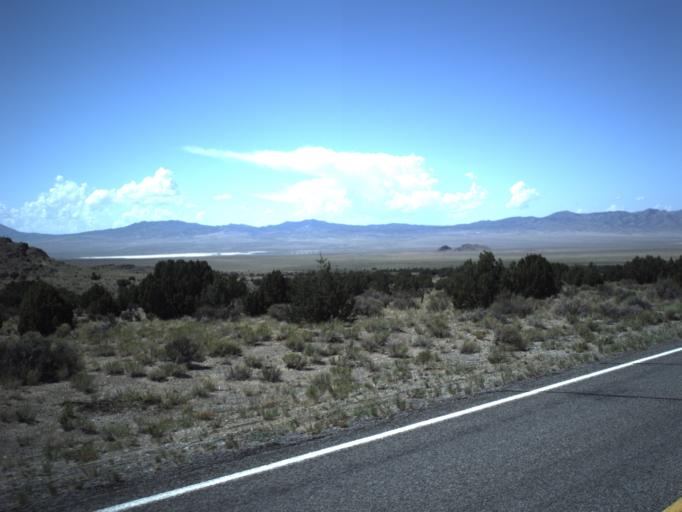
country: US
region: Utah
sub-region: Beaver County
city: Milford
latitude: 39.0770
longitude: -113.7094
